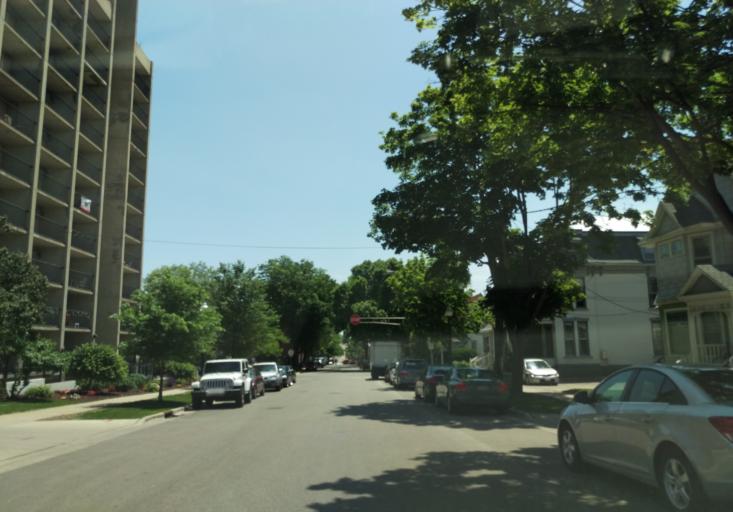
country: US
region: Wisconsin
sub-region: Dane County
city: Madison
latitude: 43.0765
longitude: -89.3922
